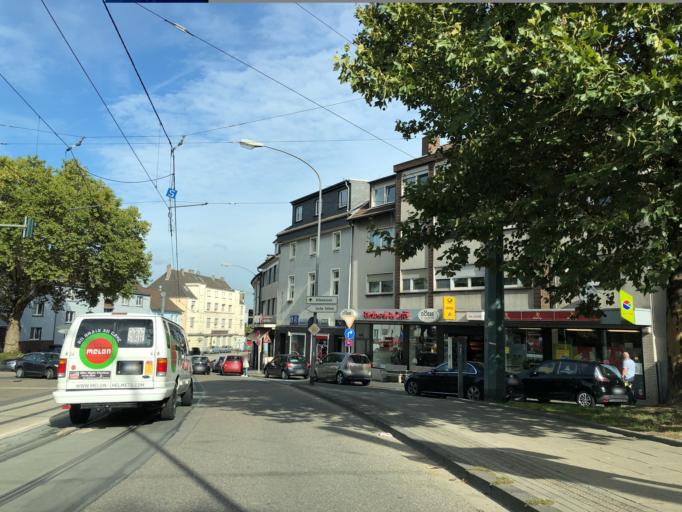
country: DE
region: North Rhine-Westphalia
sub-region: Regierungsbezirk Dusseldorf
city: Essen
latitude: 51.4767
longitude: 7.0380
